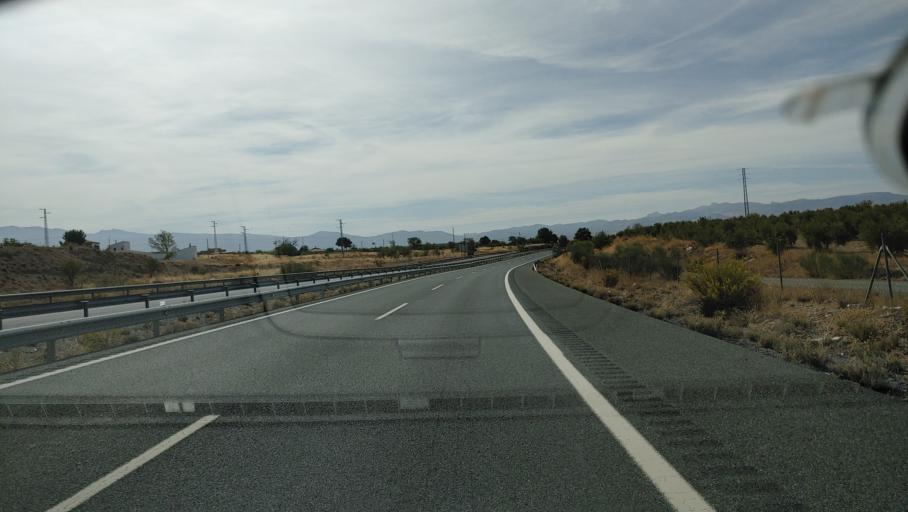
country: ES
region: Andalusia
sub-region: Provincia de Granada
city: Gor
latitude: 37.3776
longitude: -3.0617
